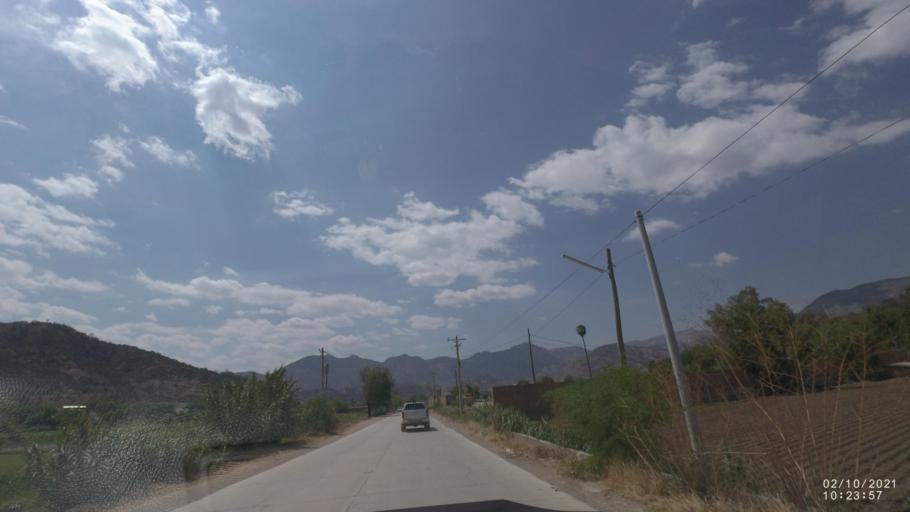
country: BO
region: Cochabamba
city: Irpa Irpa
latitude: -17.7241
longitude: -66.2781
